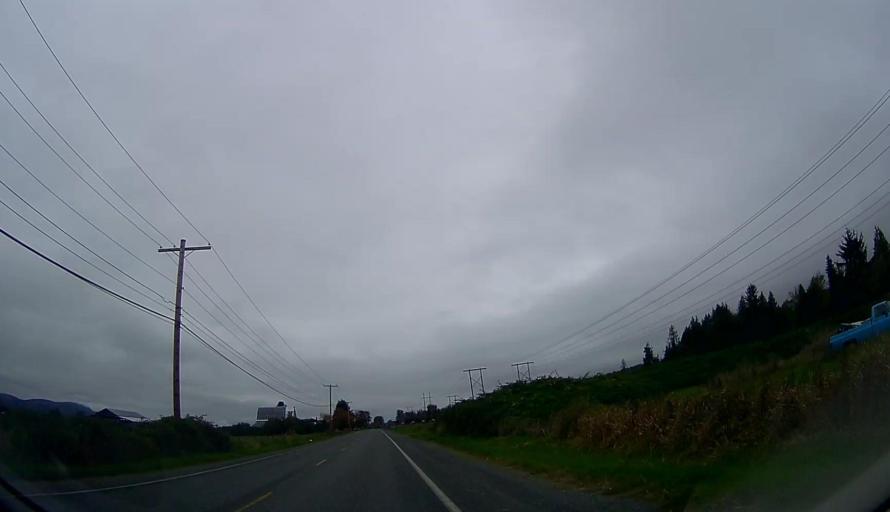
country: US
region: Washington
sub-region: Skagit County
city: Sedro-Woolley
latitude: 48.5255
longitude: -122.1335
